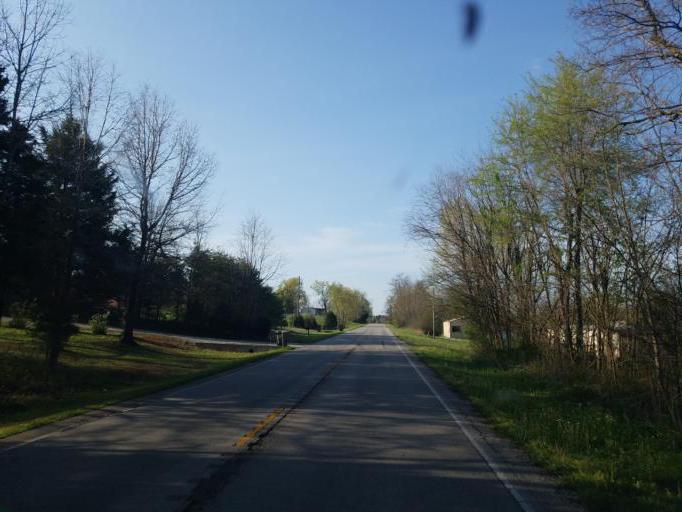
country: US
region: Kentucky
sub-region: Hart County
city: Munfordville
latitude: 37.4466
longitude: -85.8911
